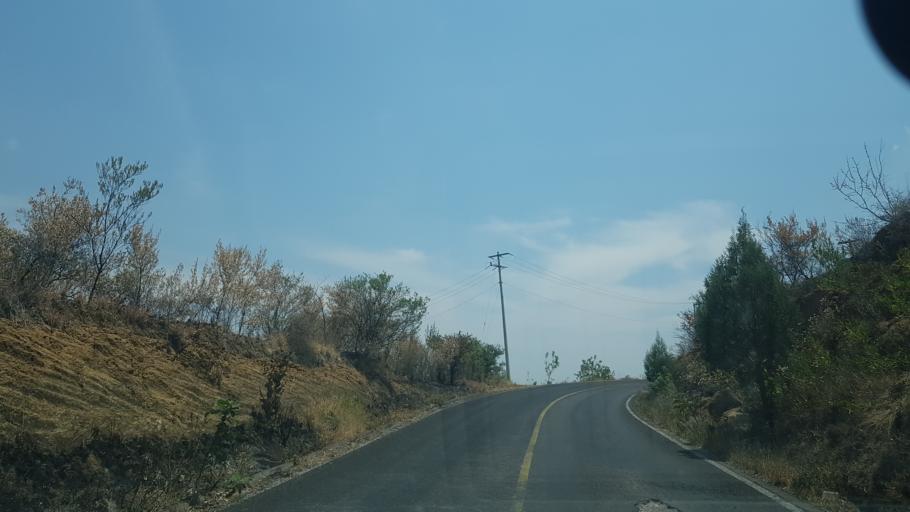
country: MX
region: Puebla
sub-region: Atzitzihuacan
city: Santiago Atzitzihuacan
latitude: 18.8347
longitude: -98.5881
